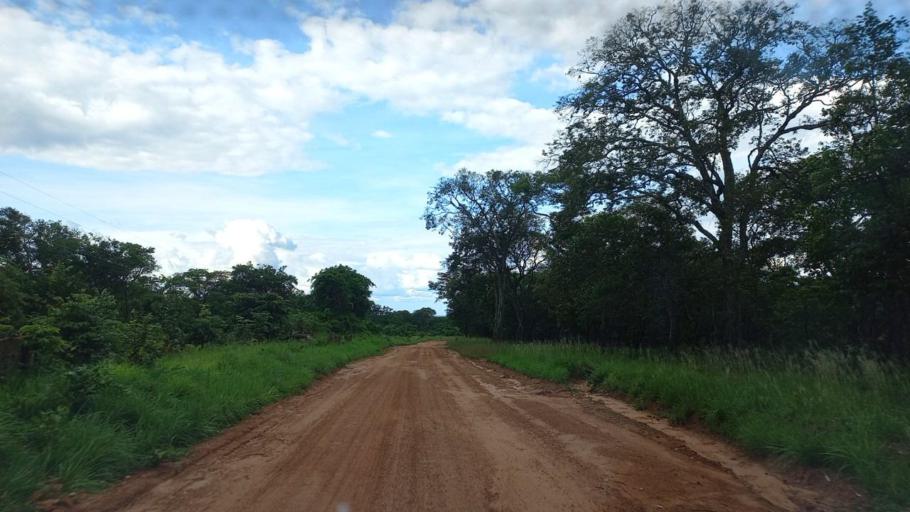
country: ZM
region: North-Western
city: Mwinilunga
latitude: -11.8173
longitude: 24.3644
